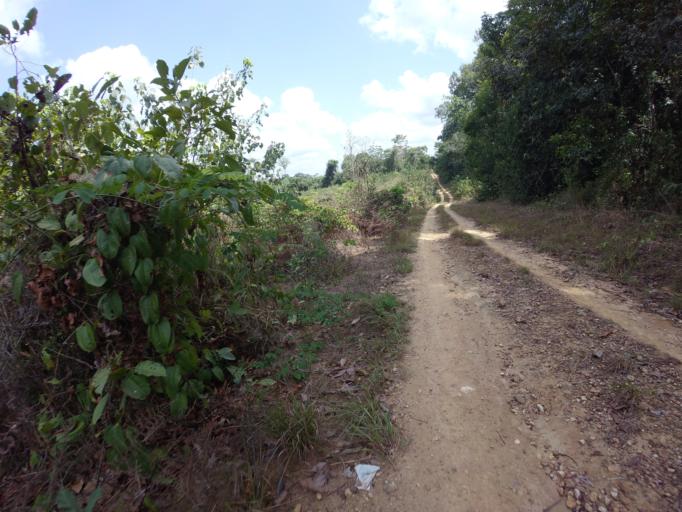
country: SL
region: Eastern Province
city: Jojoima
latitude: 7.7651
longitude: -10.5401
